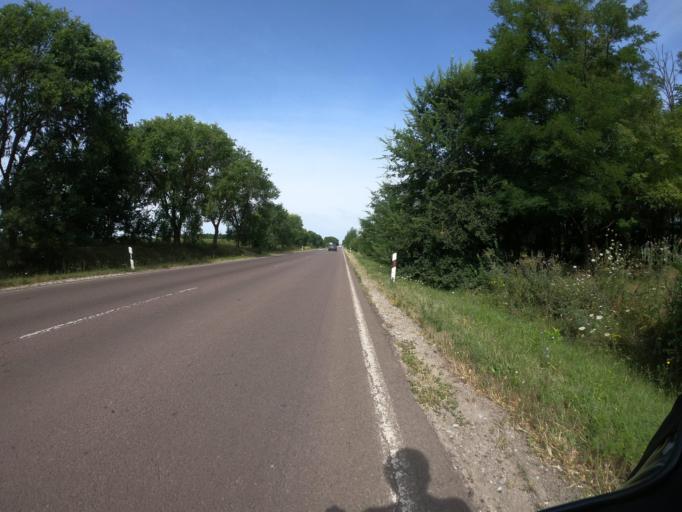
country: HU
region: Jasz-Nagykun-Szolnok
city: Tiszafured
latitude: 47.6038
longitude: 20.7851
